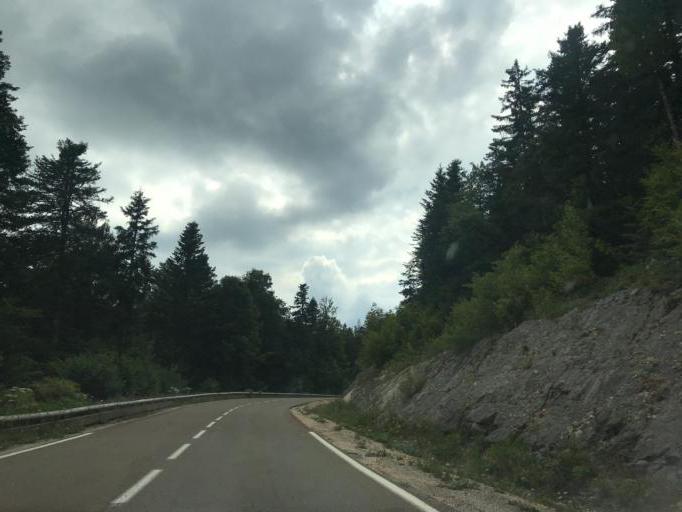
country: FR
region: Franche-Comte
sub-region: Departement du Jura
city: Longchaumois
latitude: 46.4967
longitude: 5.9245
